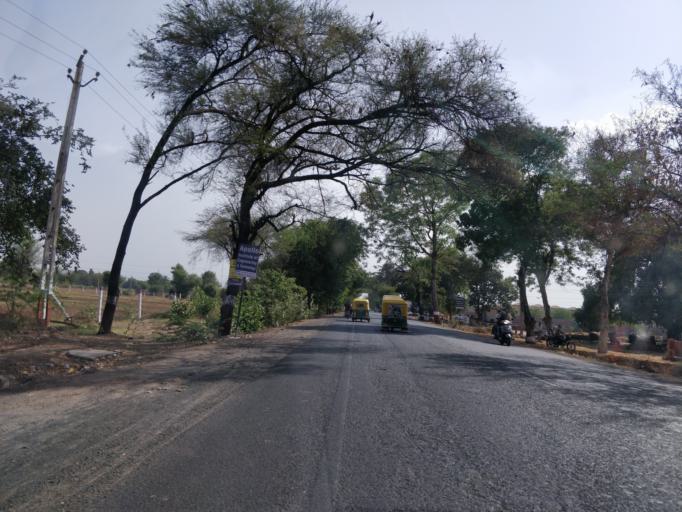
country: IN
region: Gujarat
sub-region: Ahmadabad
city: Naroda
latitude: 23.0948
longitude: 72.6958
